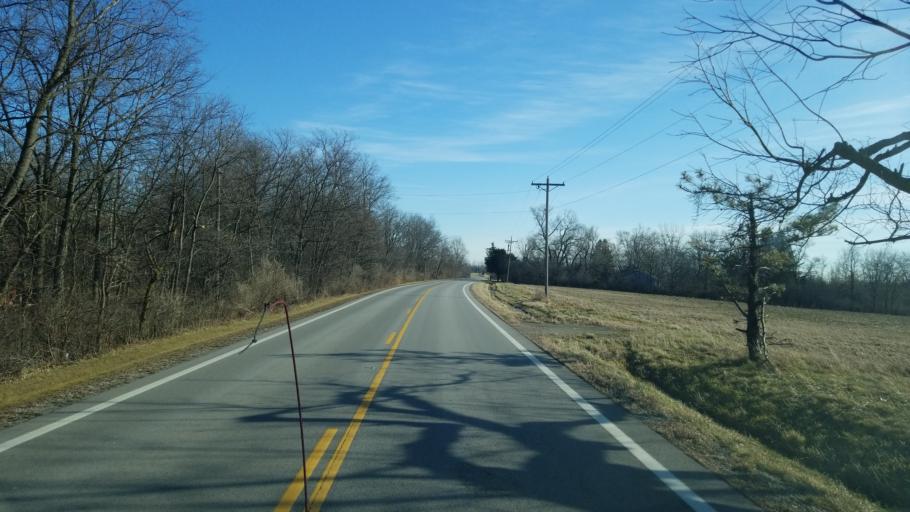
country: US
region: Ohio
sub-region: Henry County
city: Liberty Center
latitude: 41.4128
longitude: -83.8951
